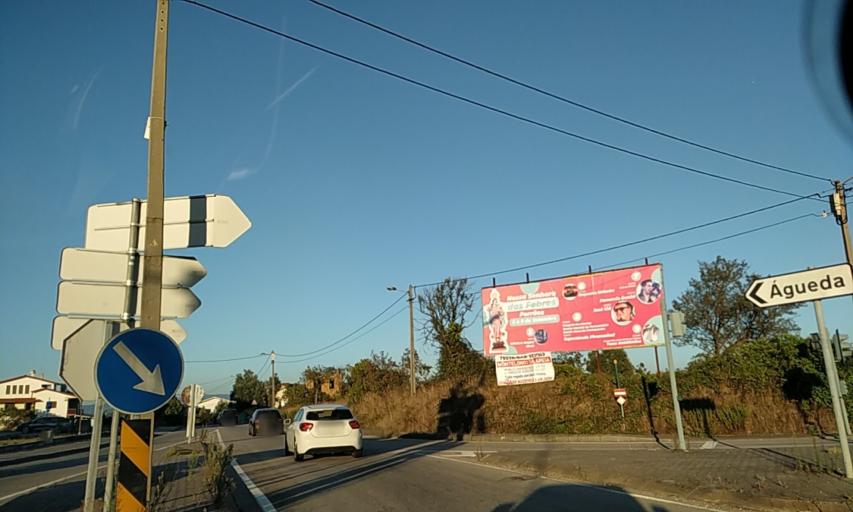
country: PT
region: Aveiro
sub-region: Oliveira do Bairro
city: Oia
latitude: 40.5430
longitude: -8.5327
